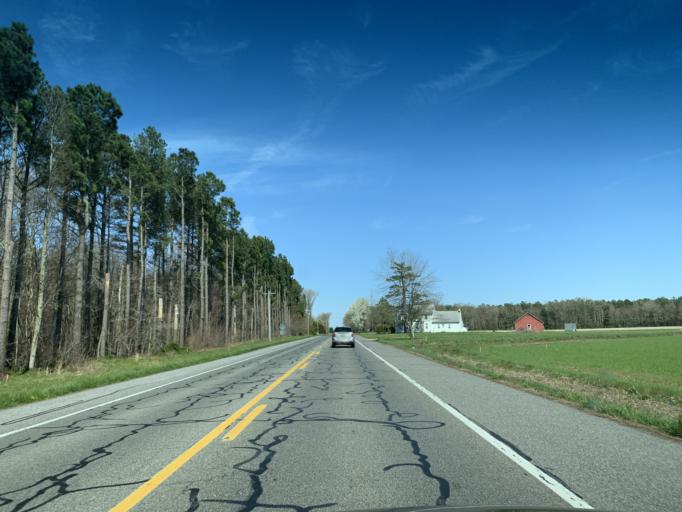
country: US
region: Delaware
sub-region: Kent County
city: Harrington
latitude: 38.9015
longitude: -75.6223
